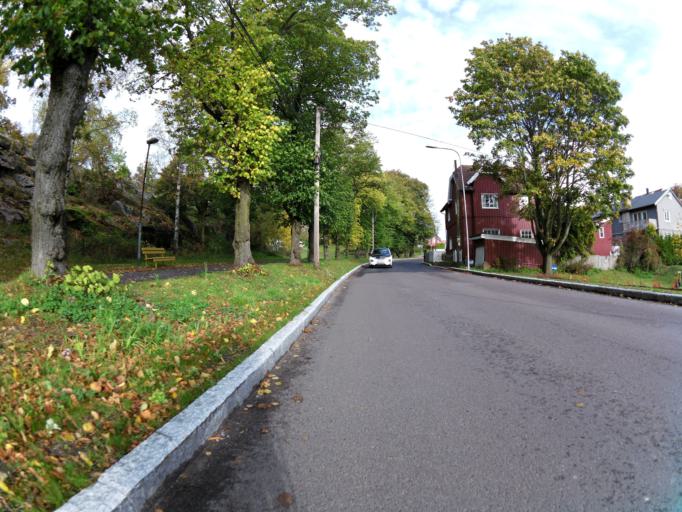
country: NO
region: Ostfold
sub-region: Fredrikstad
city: Fredrikstad
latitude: 59.2204
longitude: 10.9431
